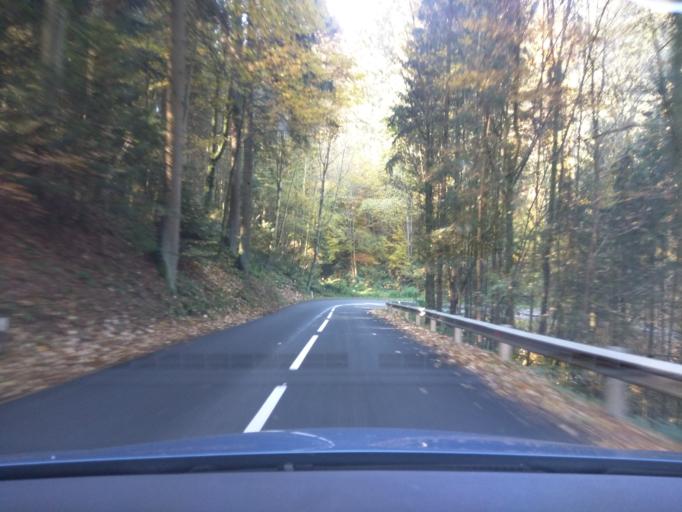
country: DE
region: Bavaria
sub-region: Lower Bavaria
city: Thyrnau
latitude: 48.5615
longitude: 13.5600
